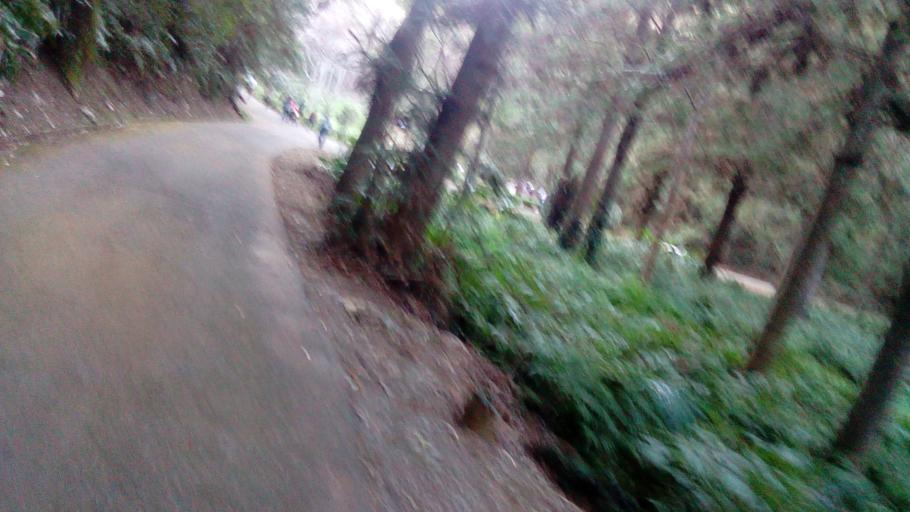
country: TW
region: Taiwan
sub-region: Nantou
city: Puli
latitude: 24.0927
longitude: 121.0326
